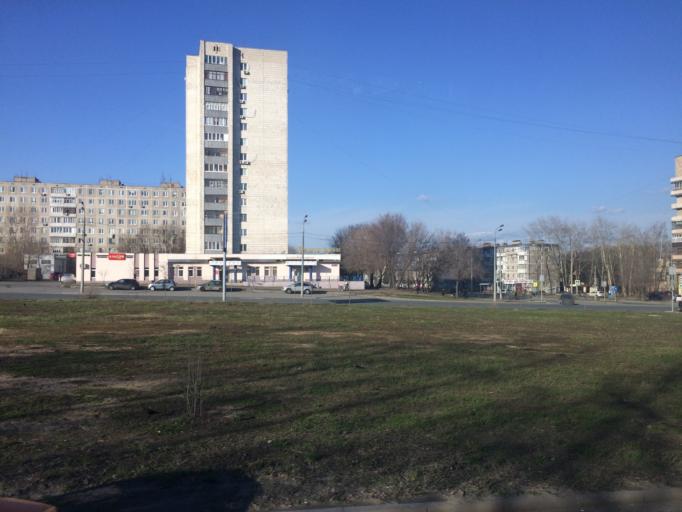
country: RU
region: Tatarstan
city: Staroye Arakchino
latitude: 55.8218
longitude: 49.0486
